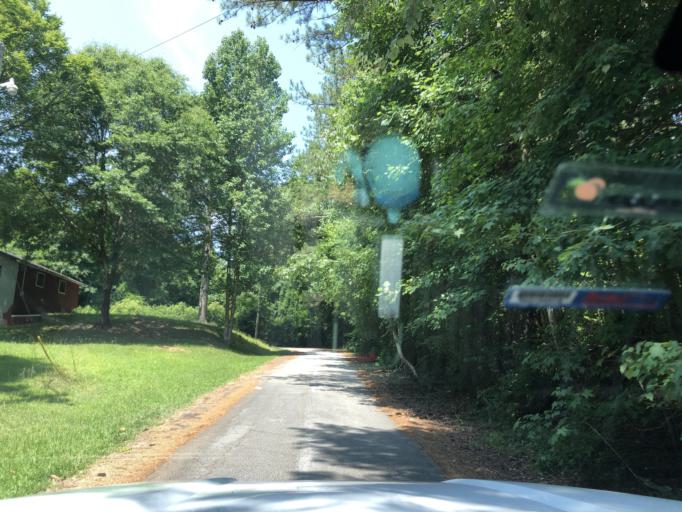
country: US
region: Georgia
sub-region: Fulton County
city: Fairburn
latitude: 33.5646
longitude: -84.5919
